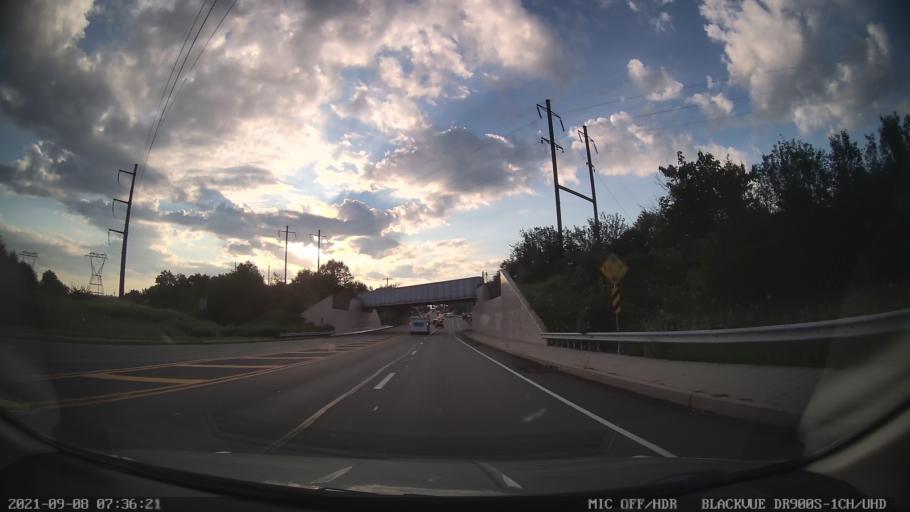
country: US
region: Pennsylvania
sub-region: Montgomery County
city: King of Prussia
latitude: 40.0837
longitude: -75.3851
